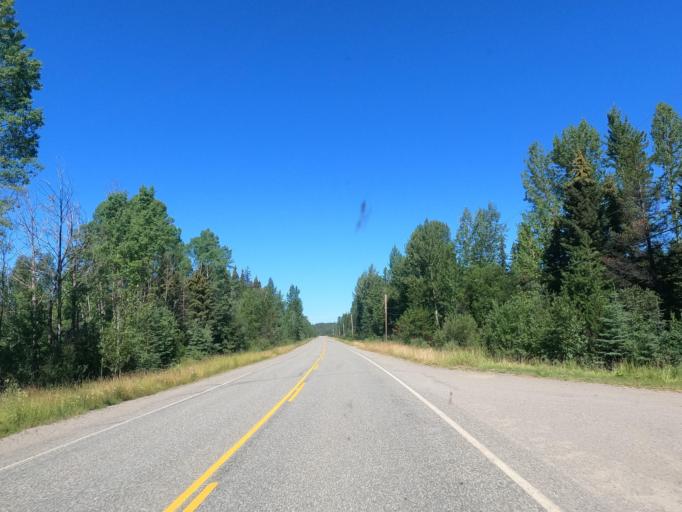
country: CA
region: British Columbia
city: Quesnel
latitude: 53.0421
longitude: -122.1400
